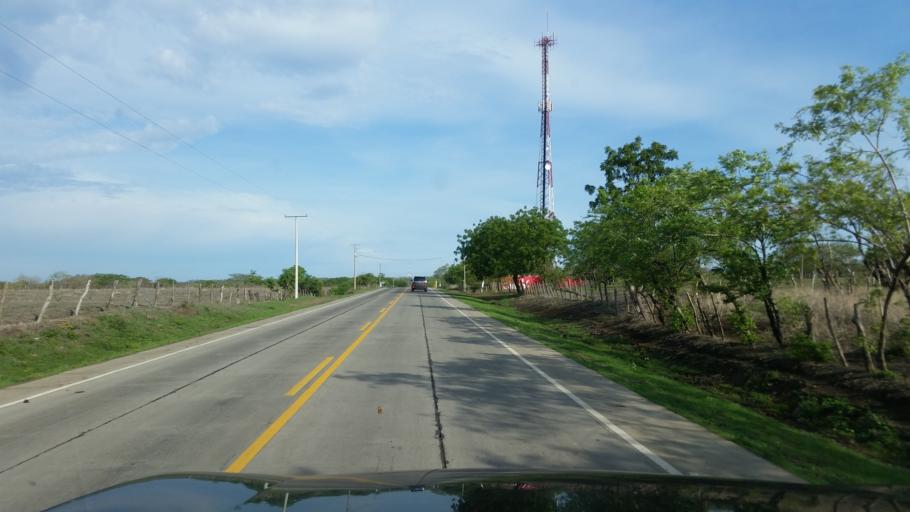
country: NI
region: Leon
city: Nagarote
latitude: 12.1107
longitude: -86.5992
